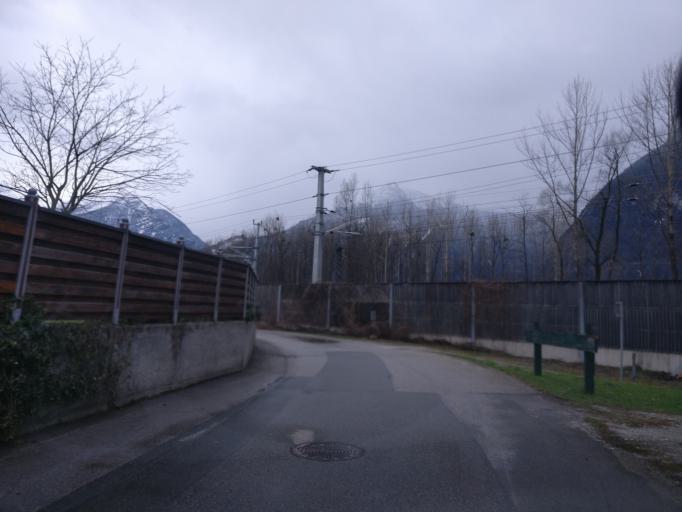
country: AT
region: Salzburg
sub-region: Politischer Bezirk Hallein
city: Golling an der Salzach
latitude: 47.6092
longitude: 13.1593
